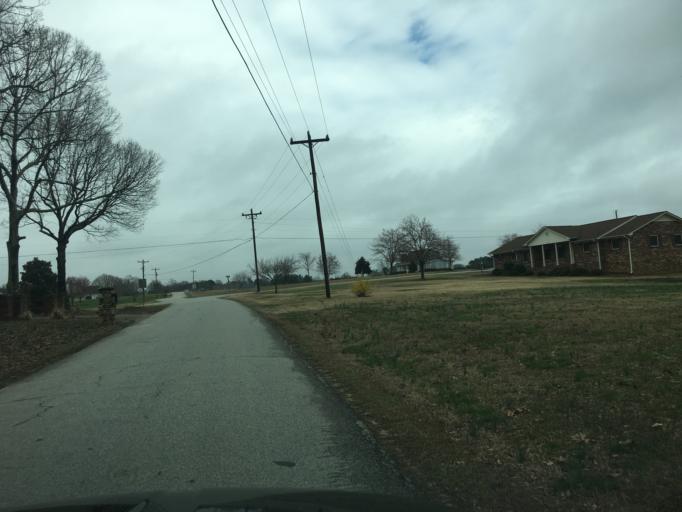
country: US
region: South Carolina
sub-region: Spartanburg County
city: Inman Mills
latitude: 35.0232
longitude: -82.1116
